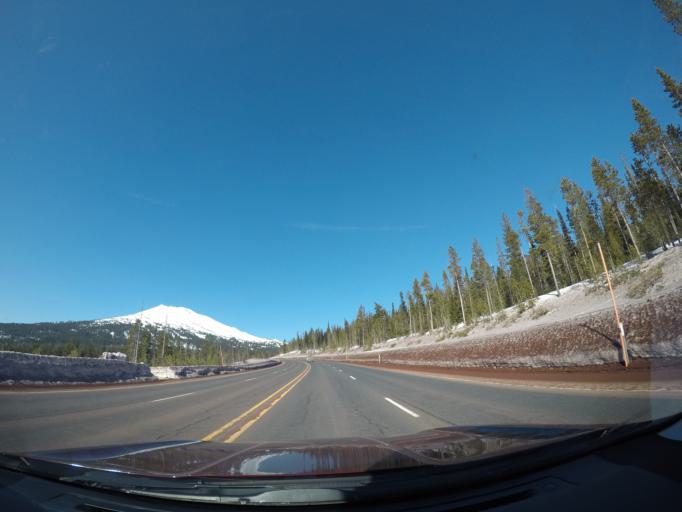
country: US
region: Oregon
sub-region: Deschutes County
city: Sunriver
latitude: 43.9839
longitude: -121.6334
